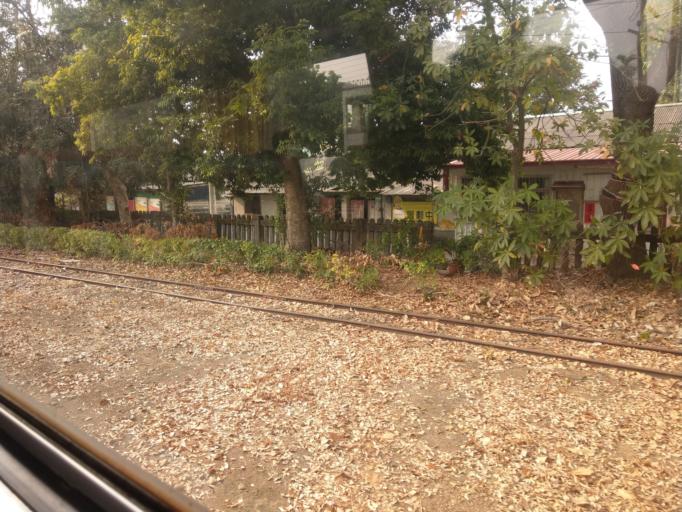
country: TW
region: Taiwan
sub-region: Chiayi
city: Jiayi Shi
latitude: 23.5260
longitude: 120.5543
